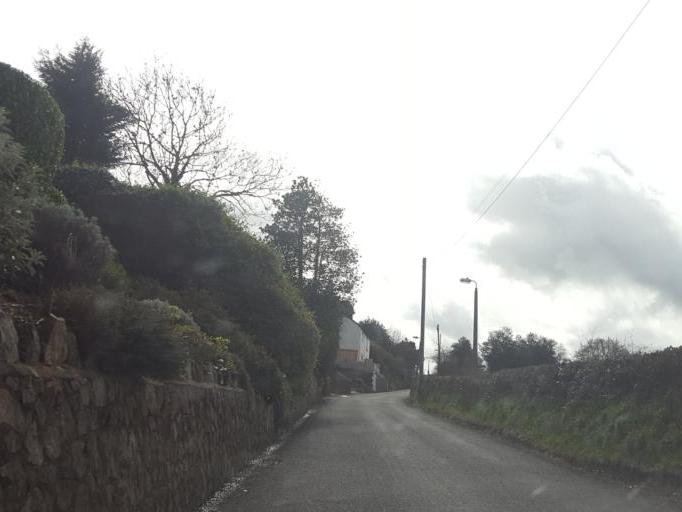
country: GB
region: England
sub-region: Worcestershire
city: Great Malvern
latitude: 52.1236
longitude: -2.3442
